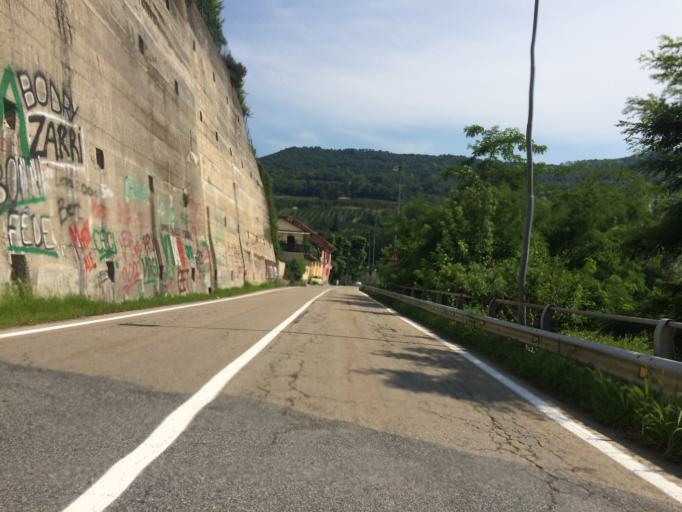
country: IT
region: Piedmont
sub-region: Provincia di Cuneo
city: Cortemilia
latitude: 44.5799
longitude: 8.1868
